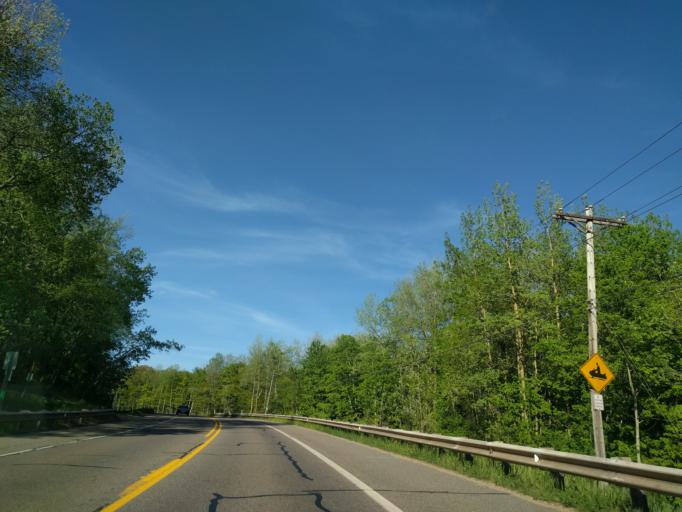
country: US
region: Michigan
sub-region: Marquette County
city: Marquette
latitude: 46.5102
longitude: -87.4157
